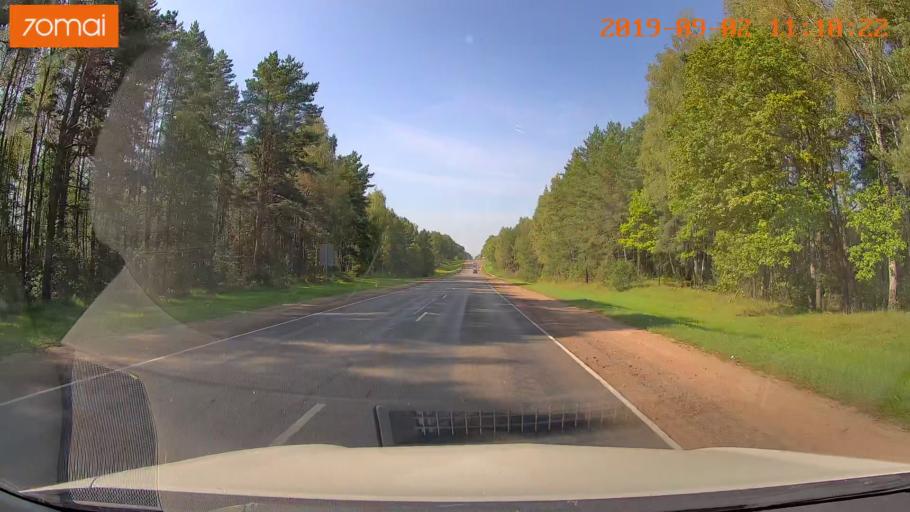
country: RU
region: Smolensk
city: Yekimovichi
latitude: 54.0990
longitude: 33.2420
